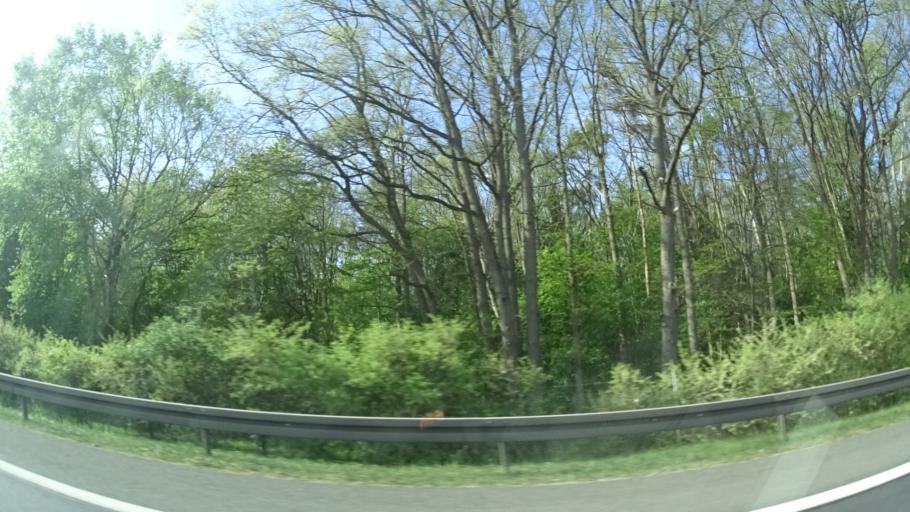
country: DE
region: Bavaria
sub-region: Regierungsbezirk Unterfranken
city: Sennfeld
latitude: 50.0270
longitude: 10.2489
